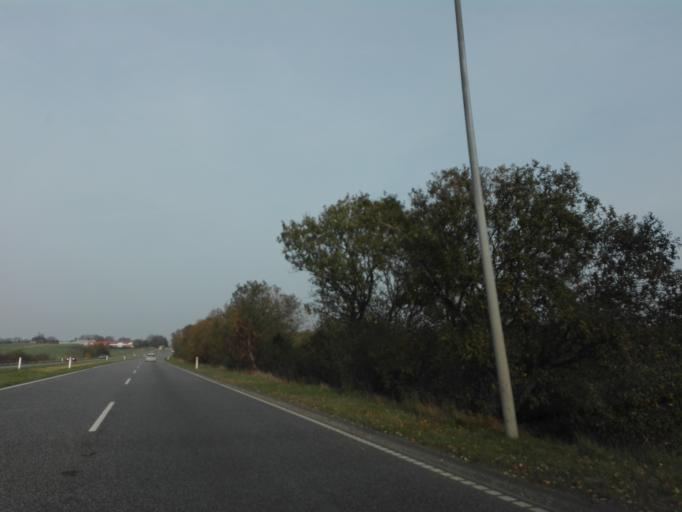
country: DK
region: Central Jutland
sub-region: Arhus Kommune
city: Solbjerg
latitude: 56.0468
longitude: 10.0817
